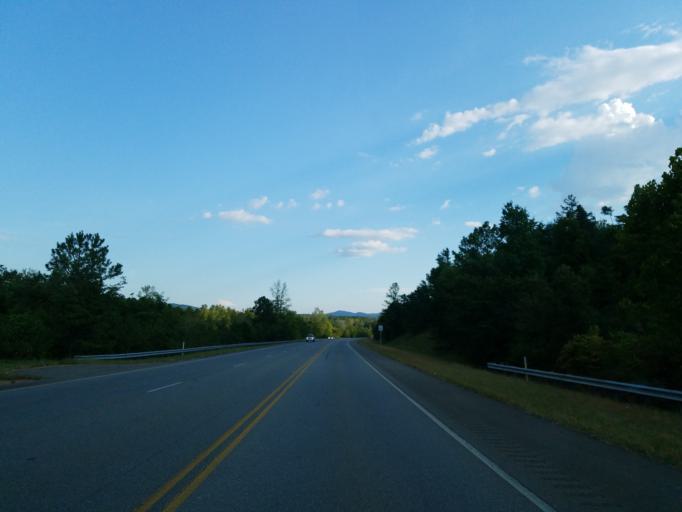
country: US
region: Georgia
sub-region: Murray County
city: Chatsworth
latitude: 34.6725
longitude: -84.7240
